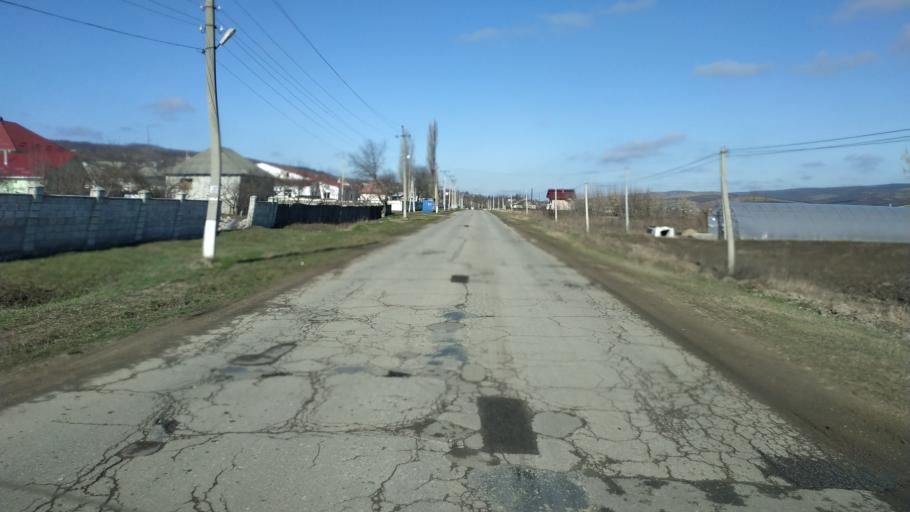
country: MD
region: Hincesti
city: Hincesti
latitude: 46.9519
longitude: 28.6111
